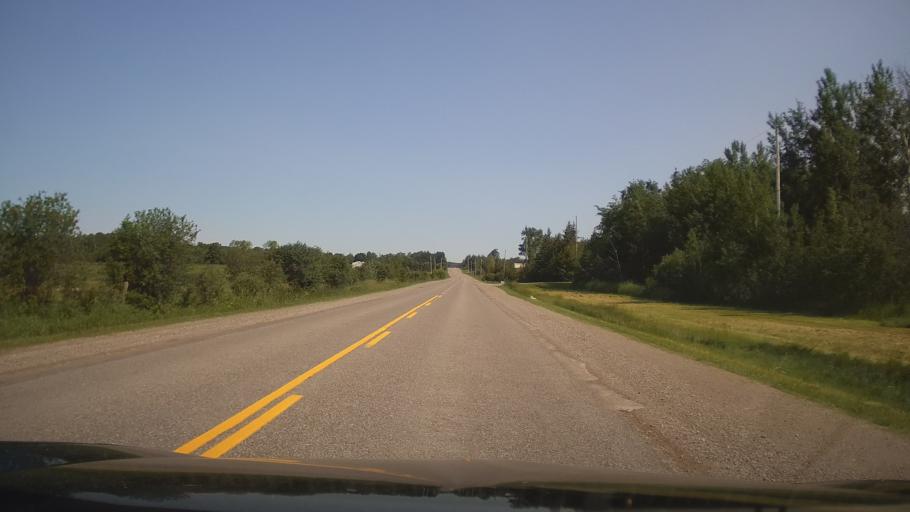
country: CA
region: Ontario
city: Omemee
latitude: 44.4586
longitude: -78.9304
